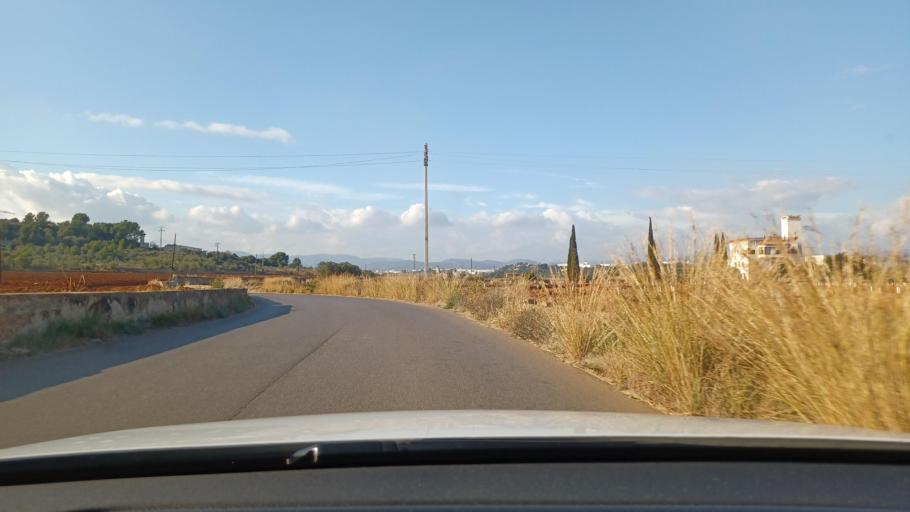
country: ES
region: Valencia
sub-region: Provincia de Castello
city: Betxi
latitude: 39.9437
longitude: -0.2150
